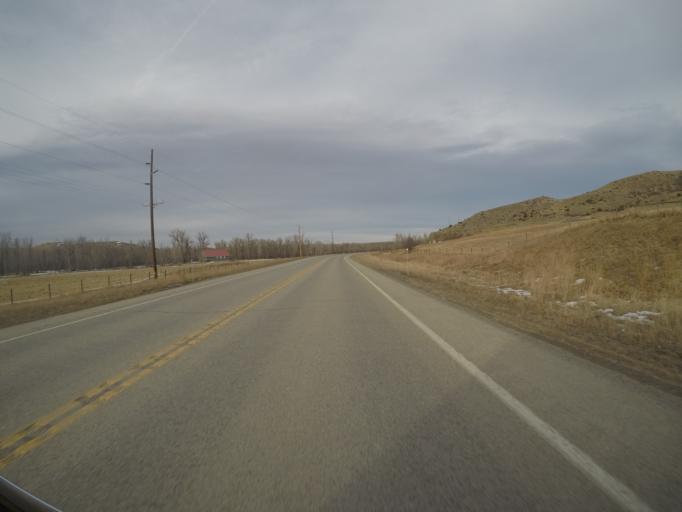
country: US
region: Montana
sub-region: Stillwater County
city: Absarokee
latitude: 45.4873
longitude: -109.4525
